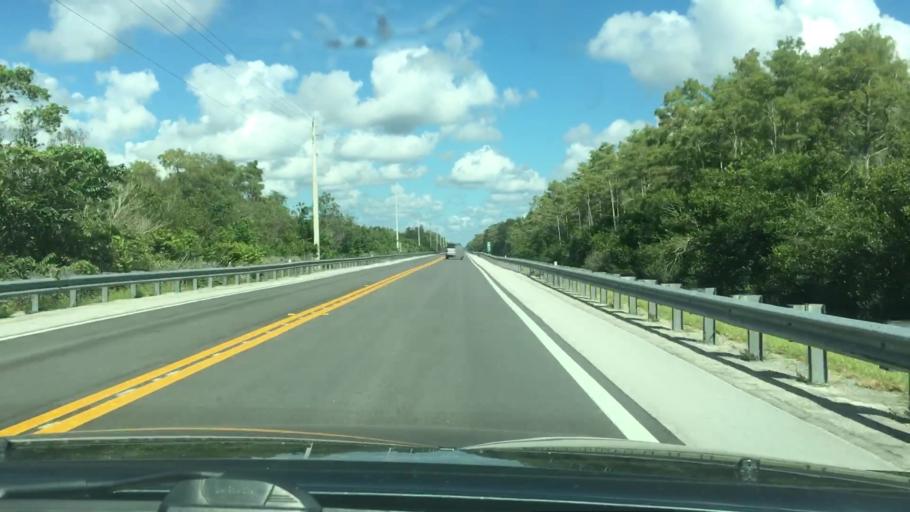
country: US
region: Florida
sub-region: Miami-Dade County
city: Kendall West
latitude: 25.7644
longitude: -80.8309
